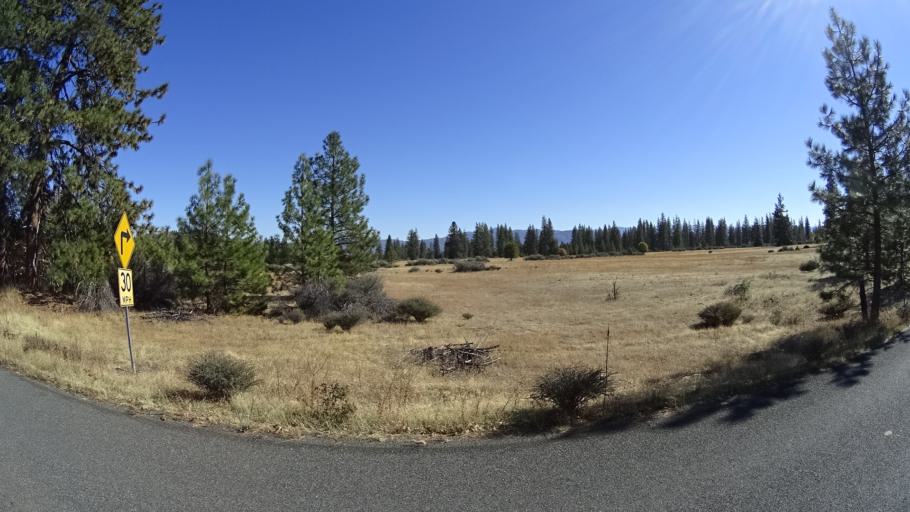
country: US
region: California
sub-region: Siskiyou County
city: Yreka
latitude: 41.5457
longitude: -122.9356
